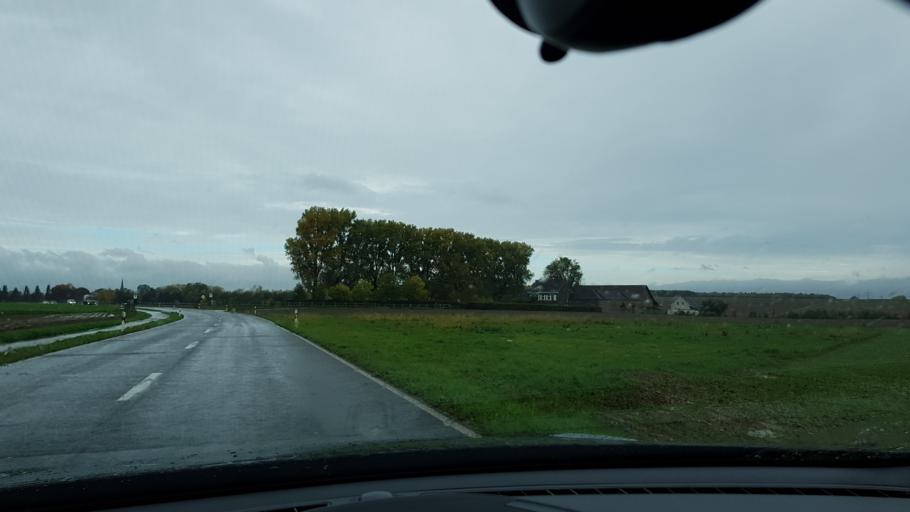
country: DE
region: North Rhine-Westphalia
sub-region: Regierungsbezirk Dusseldorf
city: Rommerskirchen
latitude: 51.0664
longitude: 6.7039
